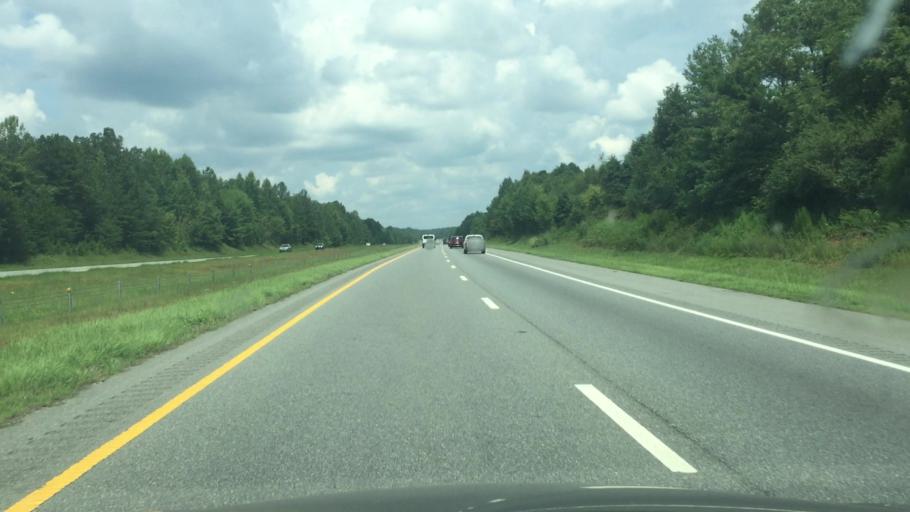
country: US
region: North Carolina
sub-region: Randolph County
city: Asheboro
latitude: 35.5638
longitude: -79.8043
